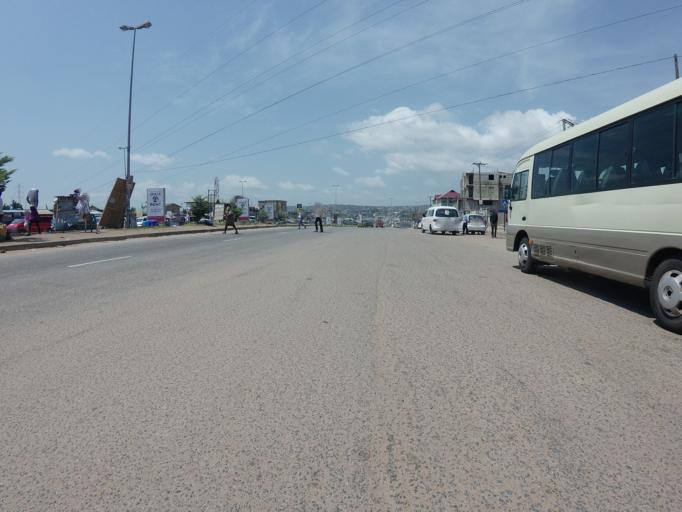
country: GH
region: Greater Accra
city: Gbawe
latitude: 5.5846
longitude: -0.2745
